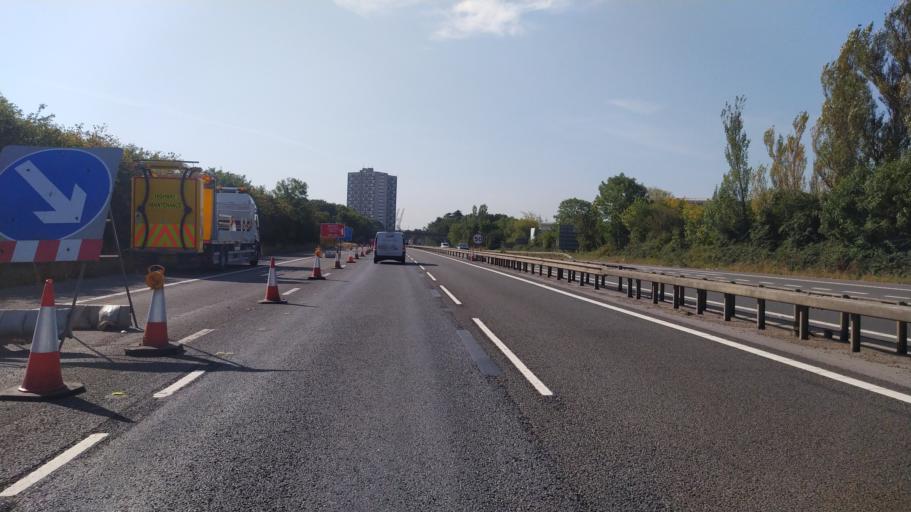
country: GB
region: England
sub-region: Hampshire
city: Totton
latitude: 50.9272
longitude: -1.4719
